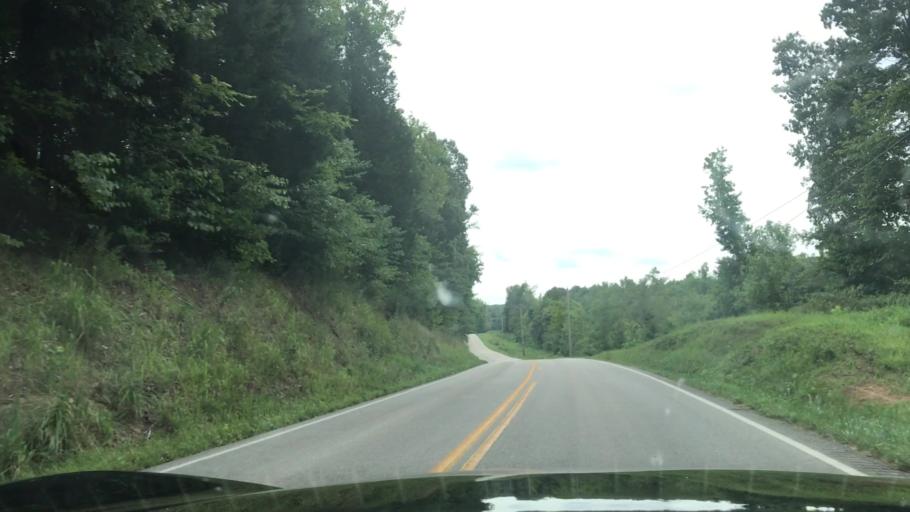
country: US
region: Kentucky
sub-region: Ohio County
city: Oak Grove
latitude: 37.2003
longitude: -86.8869
